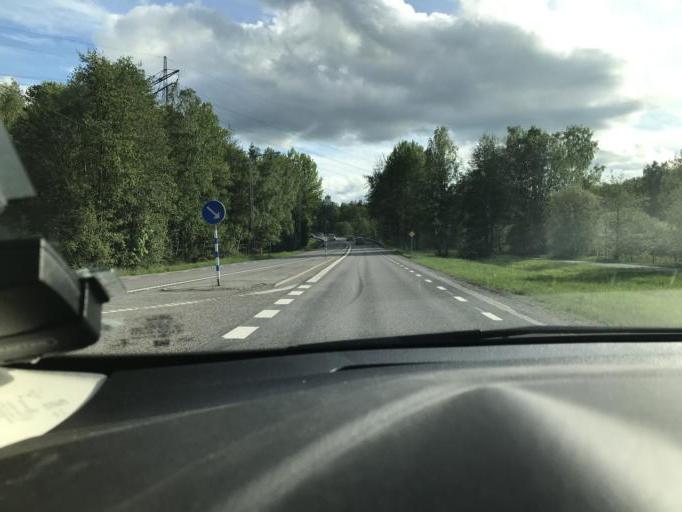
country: SE
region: Stockholm
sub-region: Botkyrka Kommun
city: Tumba
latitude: 59.2191
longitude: 17.8318
